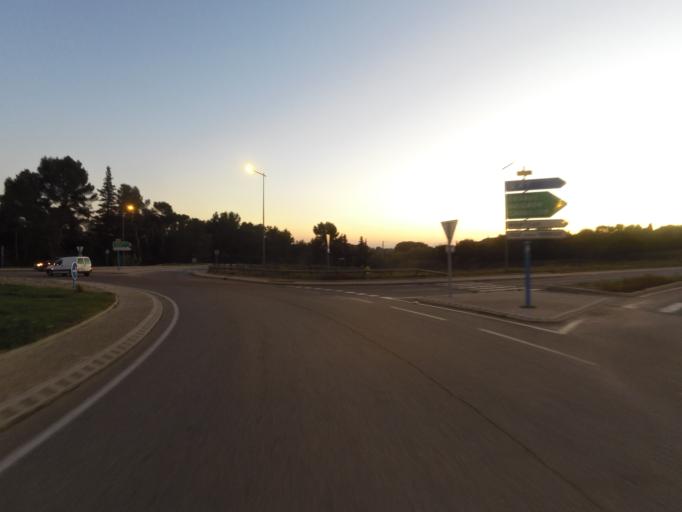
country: FR
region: Provence-Alpes-Cote d'Azur
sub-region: Departement du Vaucluse
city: Carpentras
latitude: 44.0671
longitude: 5.0673
